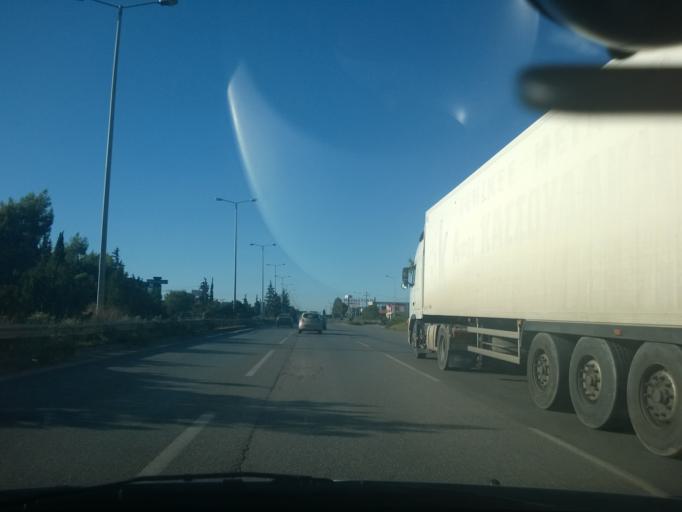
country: GR
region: Central Macedonia
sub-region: Nomos Thessalonikis
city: Pylaia
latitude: 40.5710
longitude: 22.9851
